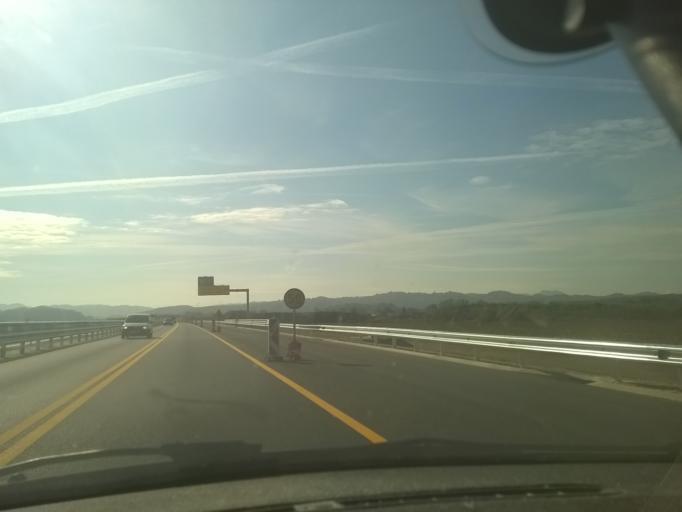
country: SI
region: Hajdina
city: Spodnja Hajdina
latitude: 46.3750
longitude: 15.8659
